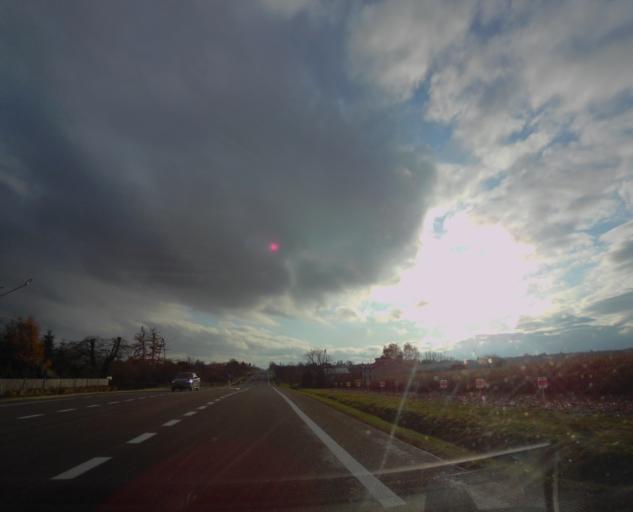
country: PL
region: Subcarpathian Voivodeship
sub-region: Powiat przemyski
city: Orly
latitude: 49.8865
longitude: 22.8160
